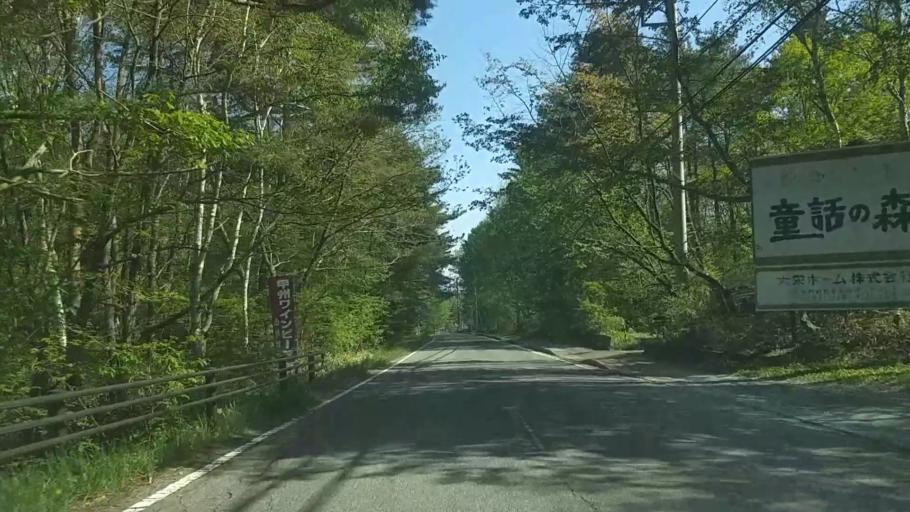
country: JP
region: Yamanashi
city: Nirasaki
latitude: 35.9111
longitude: 138.4083
